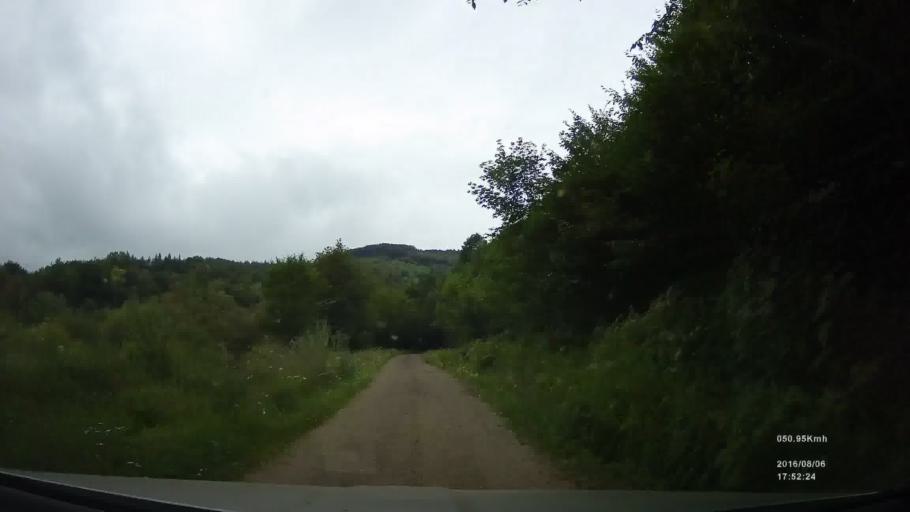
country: SK
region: Presovsky
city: Svidnik
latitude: 49.4056
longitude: 21.5673
